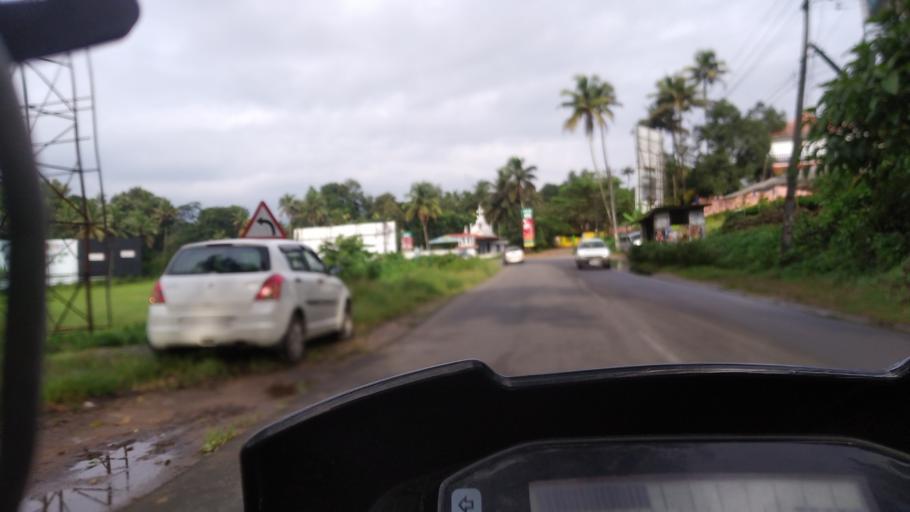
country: IN
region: Kerala
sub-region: Ernakulam
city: Kotamangalam
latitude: 10.0493
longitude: 76.7207
